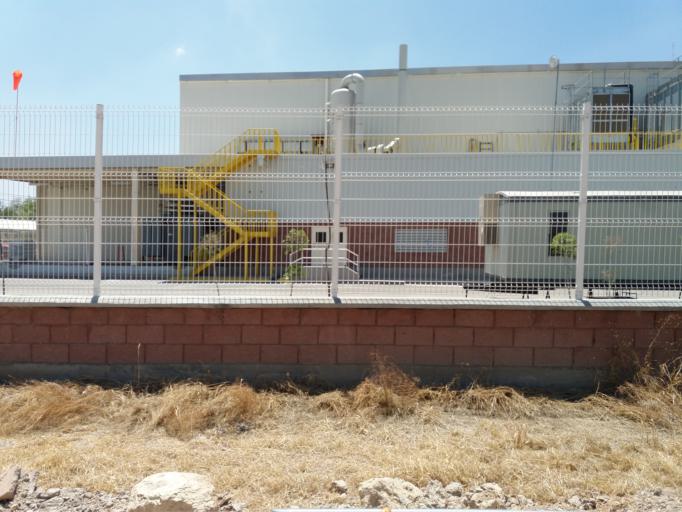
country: MX
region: Aguascalientes
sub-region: Aguascalientes
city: San Sebastian [Fraccionamiento]
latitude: 21.7996
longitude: -102.2977
